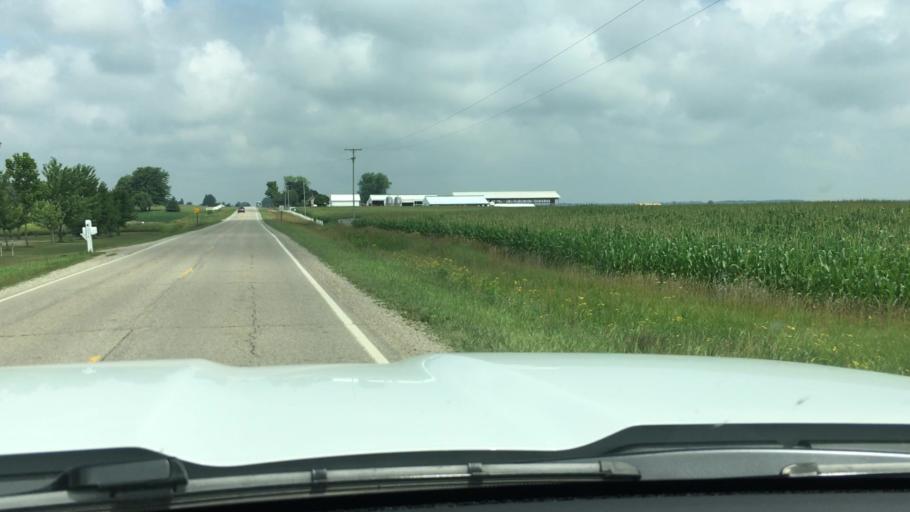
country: US
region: Michigan
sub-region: Sanilac County
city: Marlette
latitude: 43.4078
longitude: -83.0080
